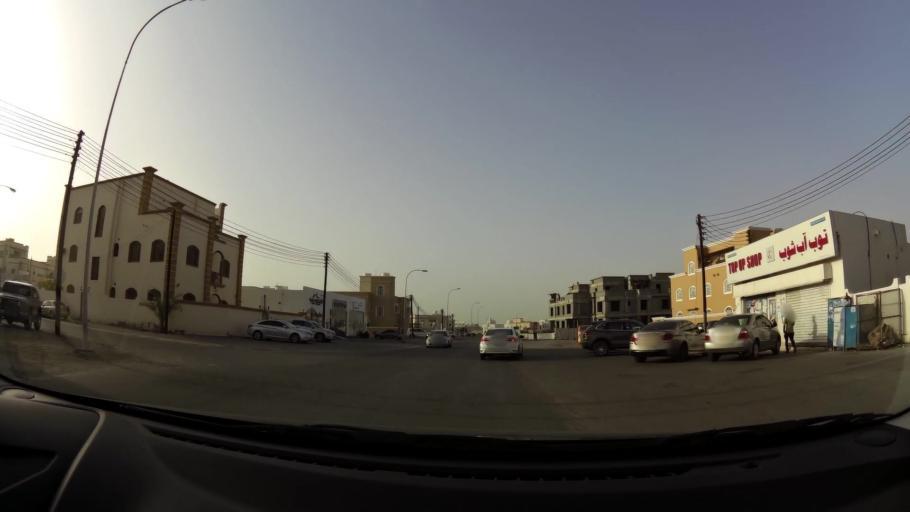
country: OM
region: Muhafazat Masqat
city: Bawshar
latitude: 23.5336
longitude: 58.3470
